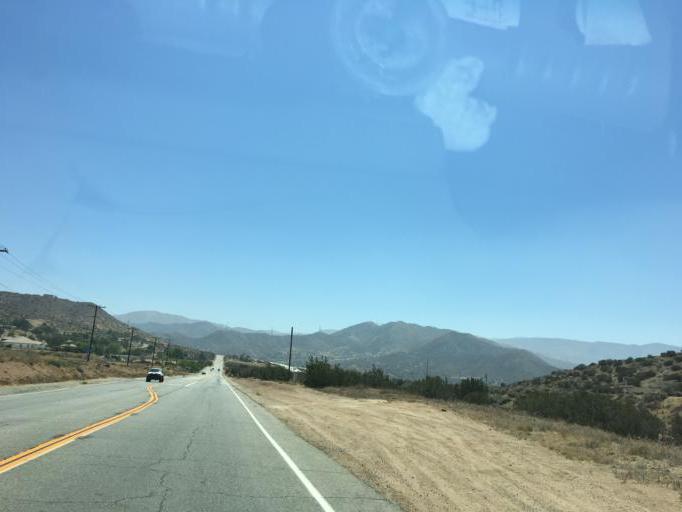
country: US
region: California
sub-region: Los Angeles County
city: Acton
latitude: 34.4926
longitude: -118.1683
